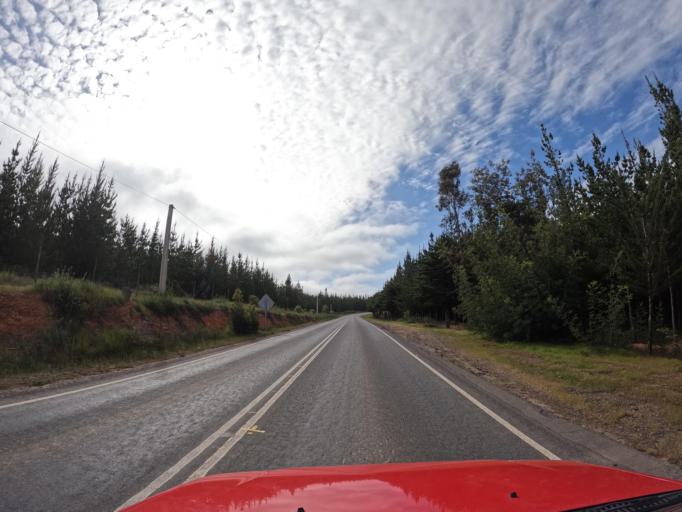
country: CL
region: O'Higgins
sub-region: Provincia de Colchagua
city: Santa Cruz
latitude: -34.3432
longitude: -71.8741
